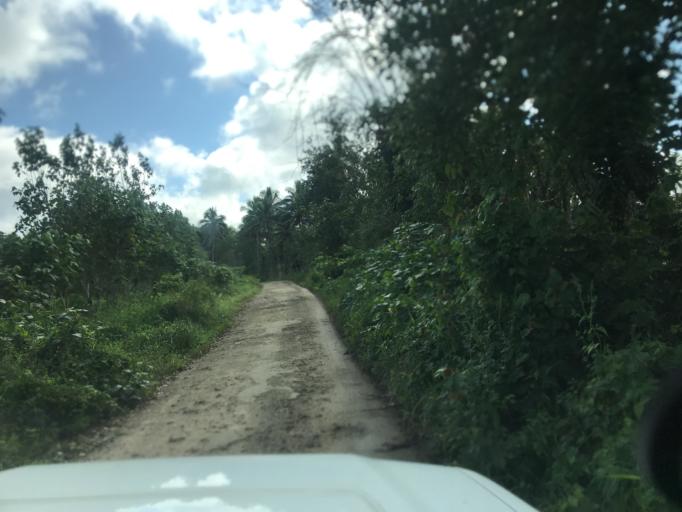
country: VU
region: Sanma
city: Luganville
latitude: -15.4704
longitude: 167.0733
